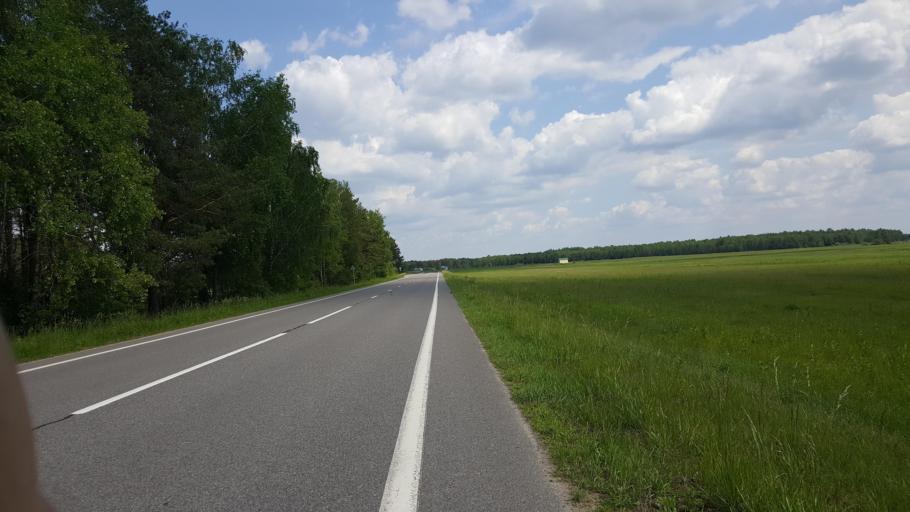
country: BY
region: Brest
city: Zhabinka
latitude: 52.4568
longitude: 24.1388
